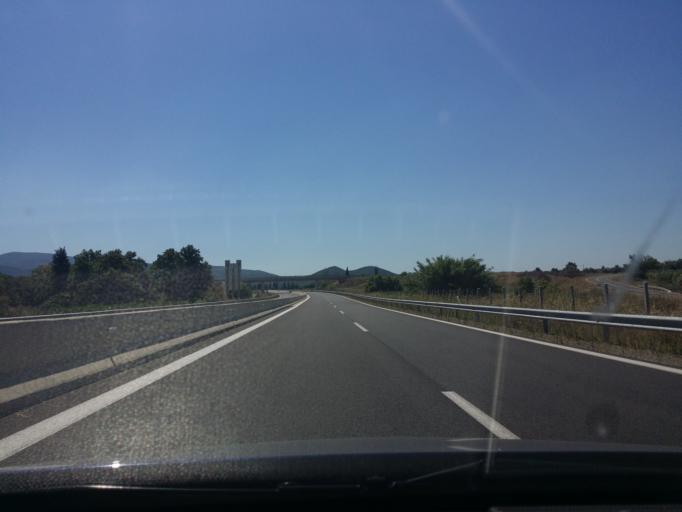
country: GR
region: Peloponnese
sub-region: Nomos Lakonias
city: Magoula
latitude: 37.1911
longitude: 22.3509
